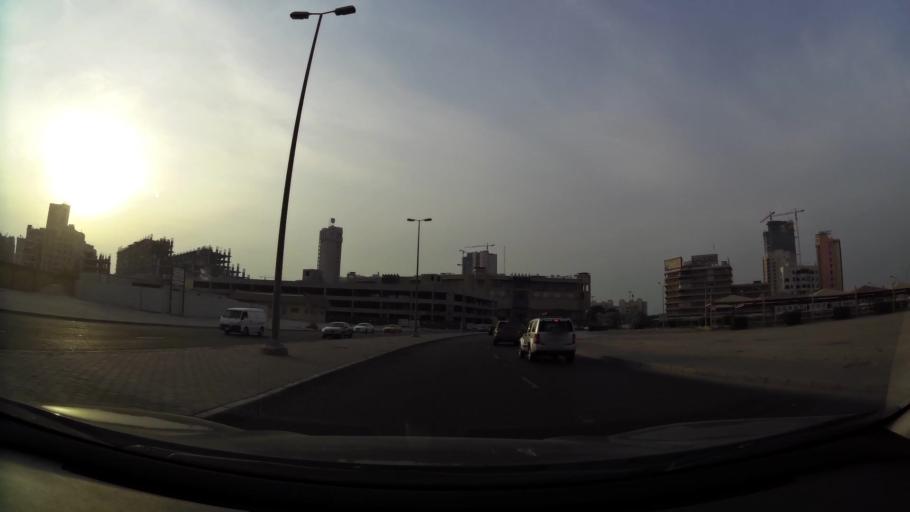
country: KW
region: Muhafazat Hawalli
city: As Salimiyah
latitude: 29.3345
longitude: 48.0655
